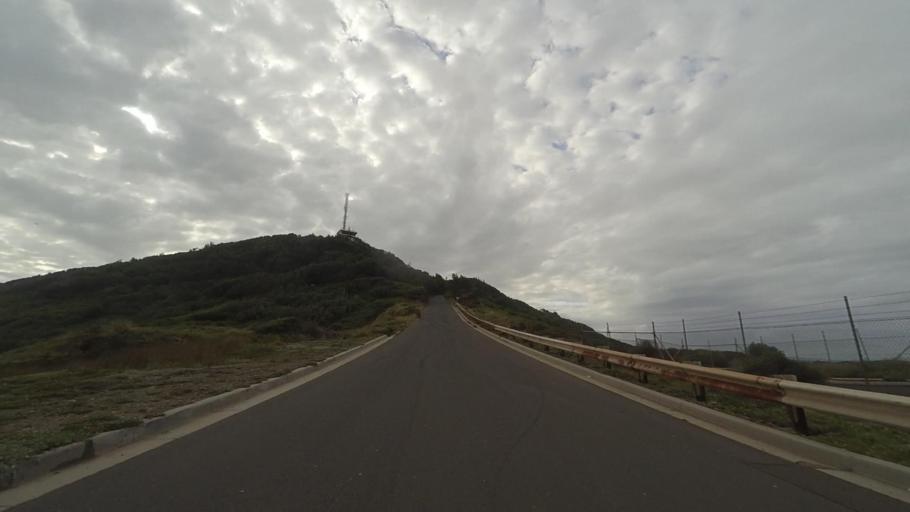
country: AU
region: New South Wales
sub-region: Wollongong
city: Port Kembla
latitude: -34.4925
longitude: 150.9185
